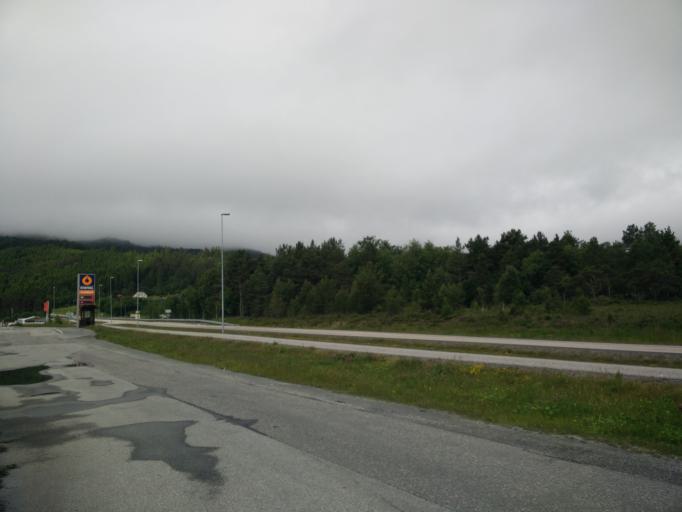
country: NO
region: More og Romsdal
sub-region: Kristiansund
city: Rensvik
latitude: 63.0117
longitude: 7.9780
